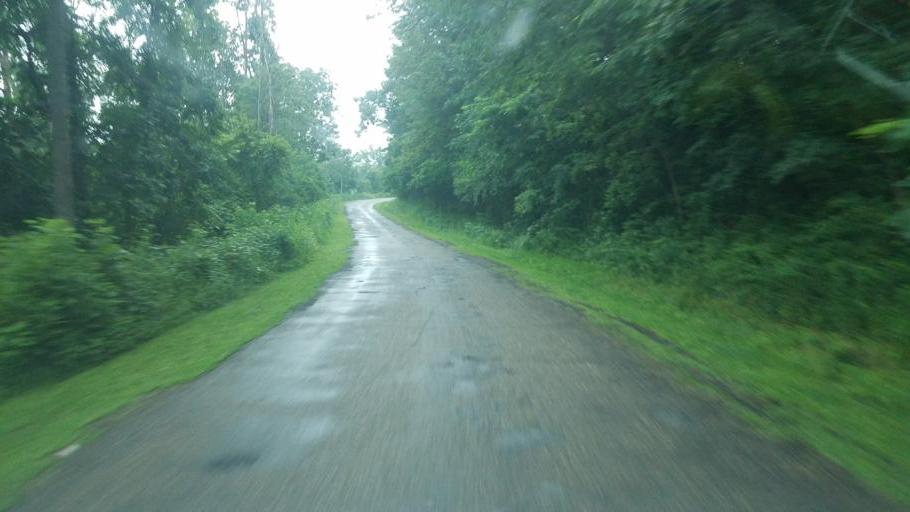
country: US
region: Ohio
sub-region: Tuscarawas County
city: Dennison
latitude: 40.3755
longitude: -81.2425
